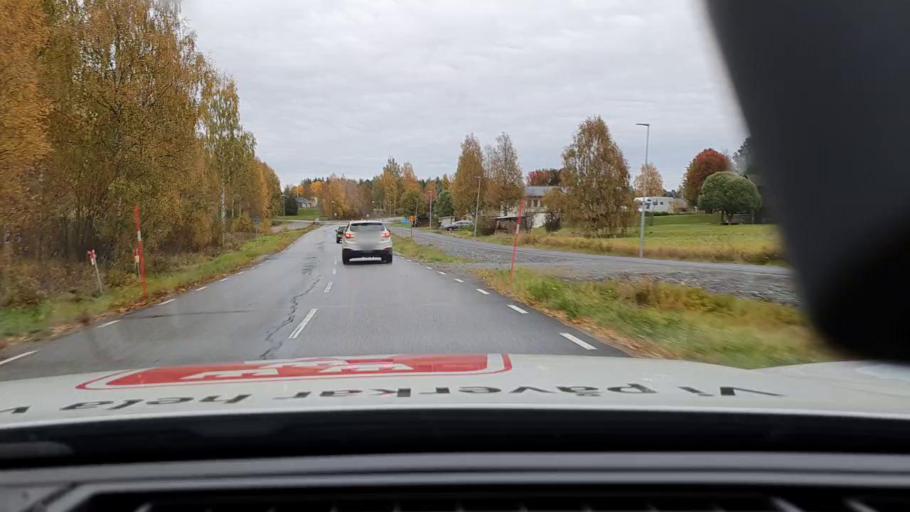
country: SE
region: Norrbotten
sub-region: Bodens Kommun
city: Saevast
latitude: 65.7686
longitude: 21.7214
